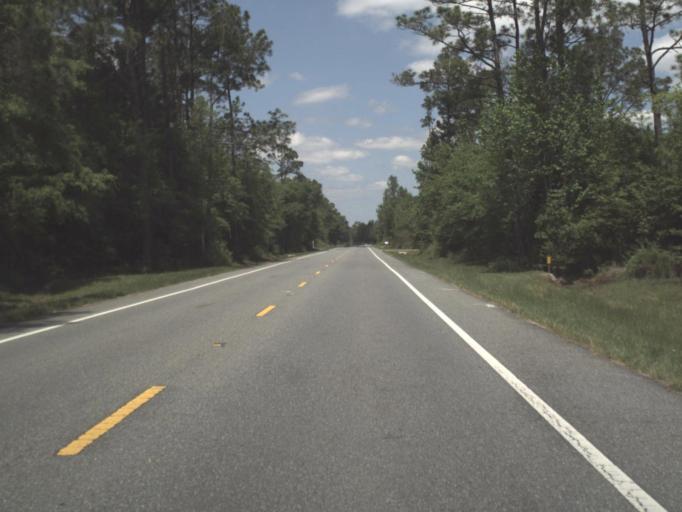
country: US
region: Florida
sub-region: Santa Rosa County
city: Point Baker
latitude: 30.7357
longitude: -87.0434
